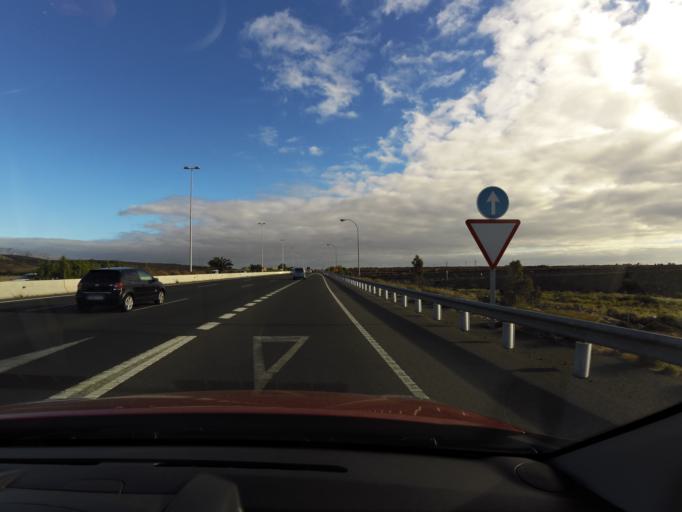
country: ES
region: Canary Islands
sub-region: Provincia de Las Palmas
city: Cruce de Arinaga
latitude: 27.8058
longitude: -15.4815
